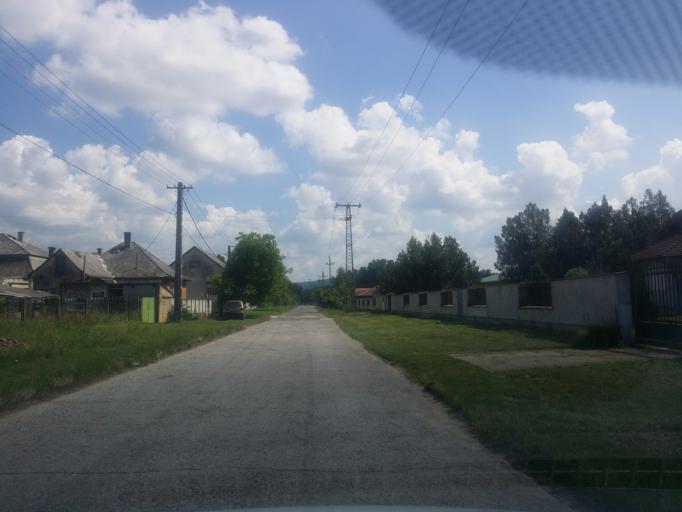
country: HU
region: Komarom-Esztergom
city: Kesztolc
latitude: 47.7110
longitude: 18.7840
